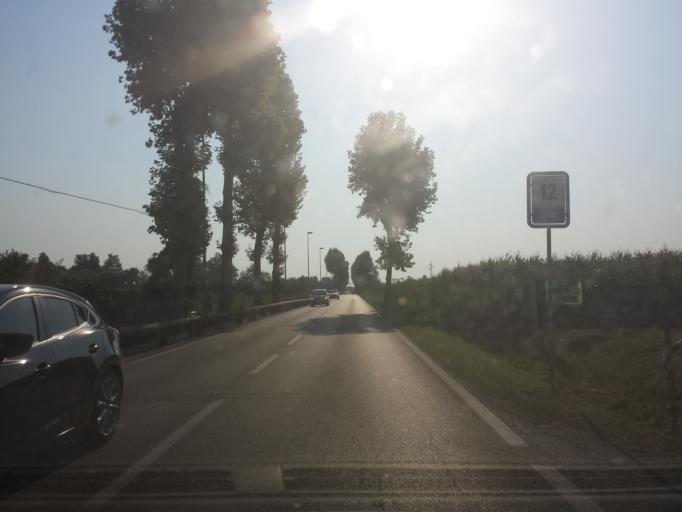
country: IT
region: Veneto
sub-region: Provincia di Venezia
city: Cavallino
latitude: 45.4826
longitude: 12.5606
